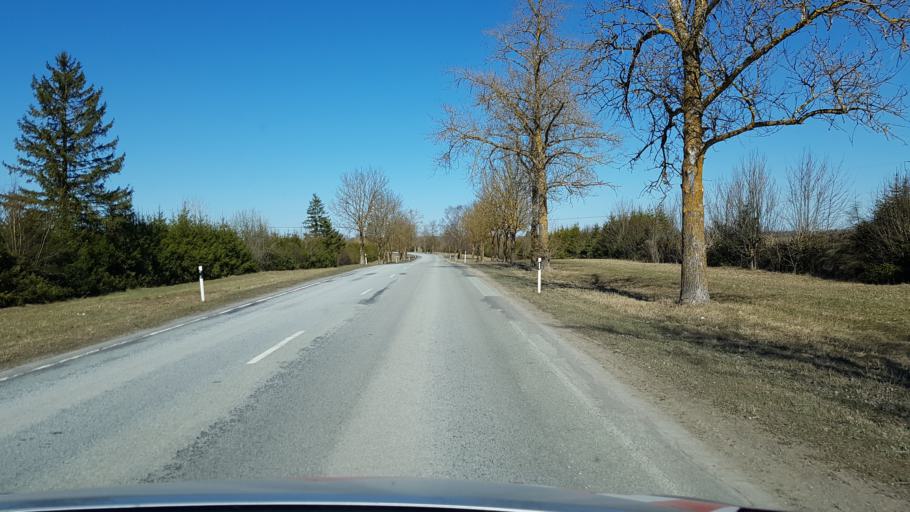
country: EE
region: Laeaene-Virumaa
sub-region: Rakvere linn
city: Rakvere
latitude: 59.3755
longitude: 26.3885
